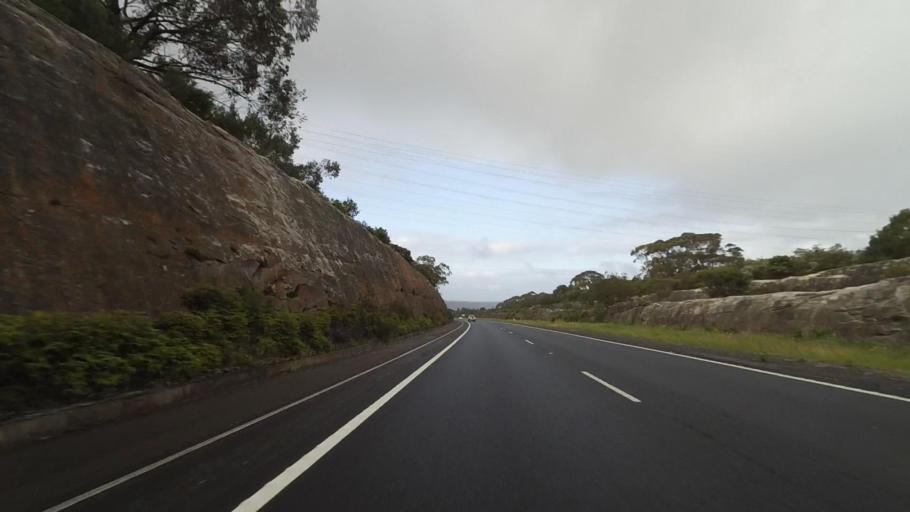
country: AU
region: New South Wales
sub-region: Wollongong
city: Helensburgh
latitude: -34.2398
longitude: 150.9450
